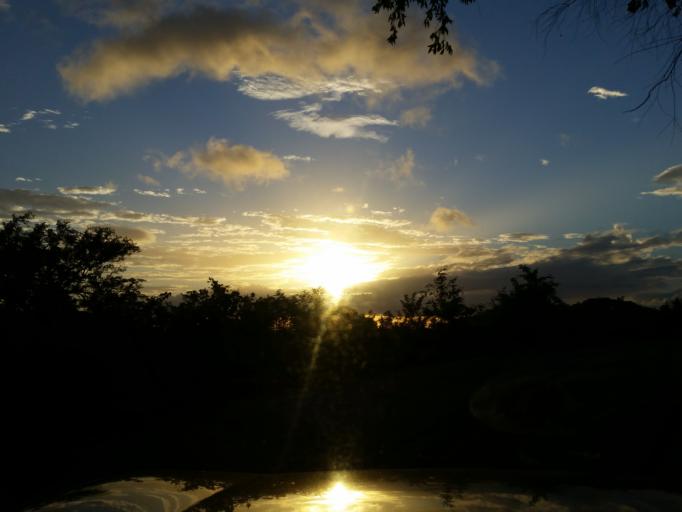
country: NI
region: Rivas
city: San Juan del Sur
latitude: 11.2657
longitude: -85.8576
